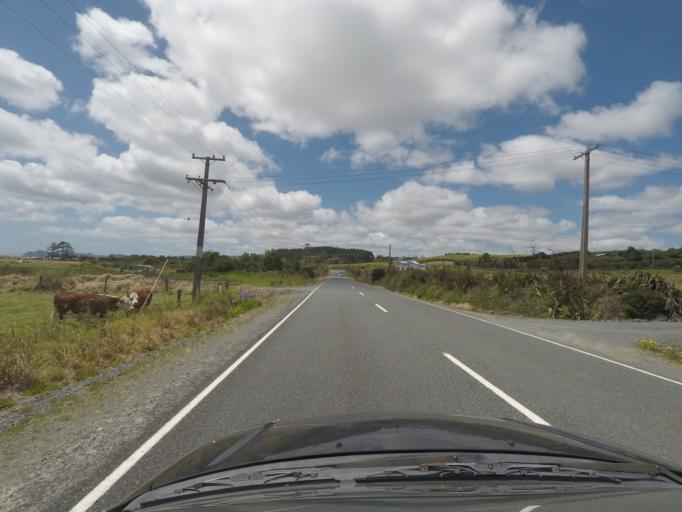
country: NZ
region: Northland
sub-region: Whangarei
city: Ruakaka
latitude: -36.0115
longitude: 174.4822
